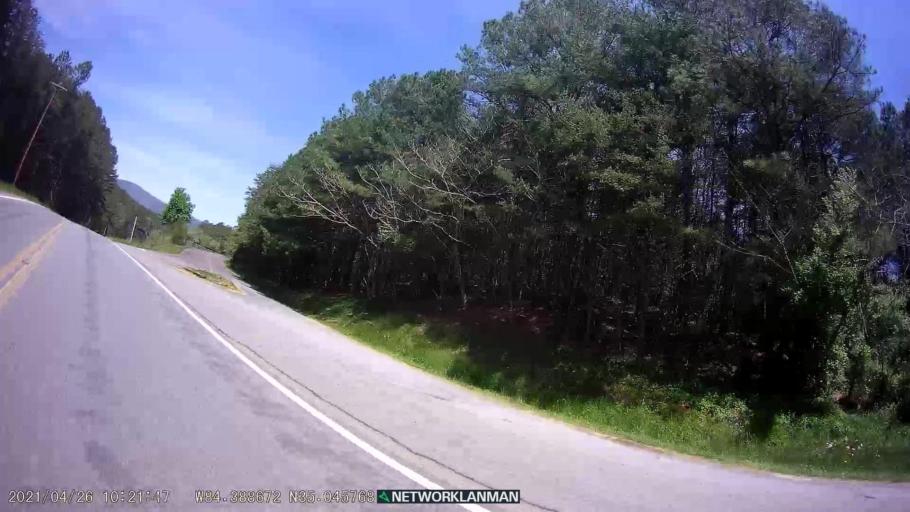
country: US
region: Georgia
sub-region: Fannin County
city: McCaysville
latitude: 35.0461
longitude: -84.3889
